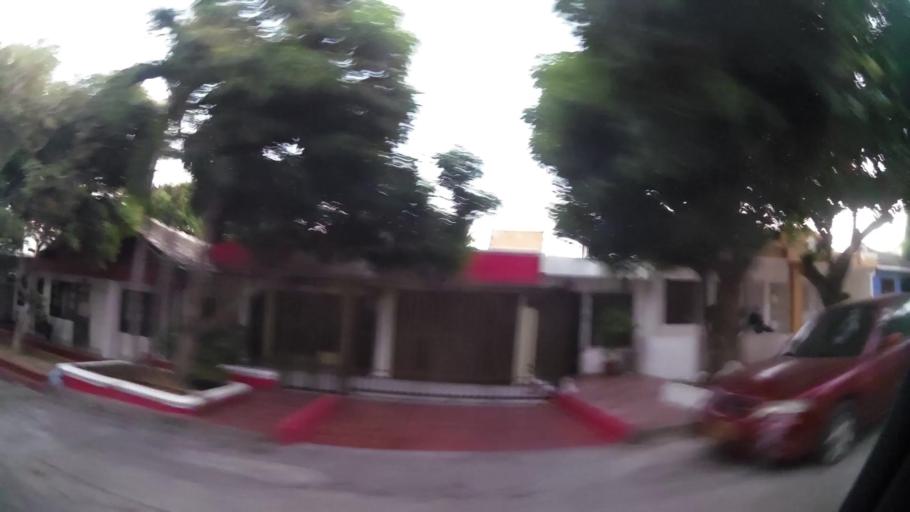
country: CO
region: Atlantico
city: Barranquilla
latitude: 10.9809
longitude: -74.8115
